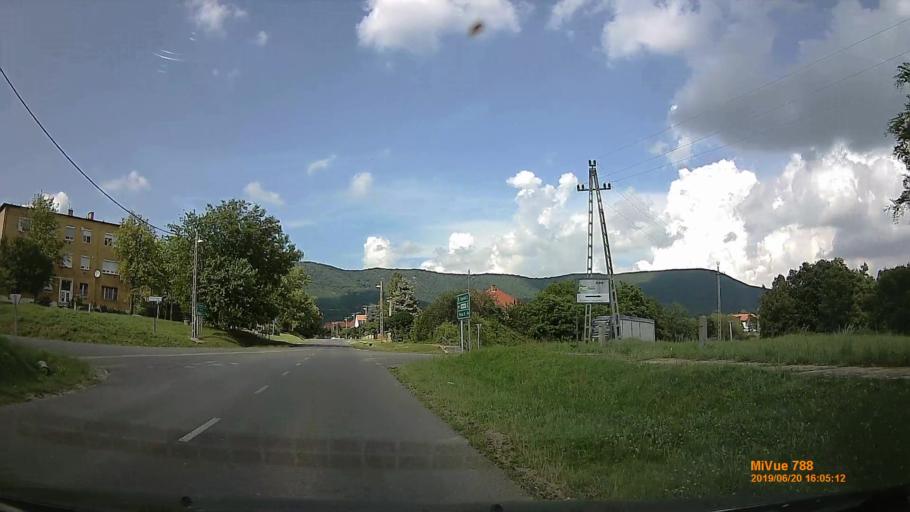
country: HU
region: Baranya
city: Pellerd
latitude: 46.0777
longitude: 18.1175
